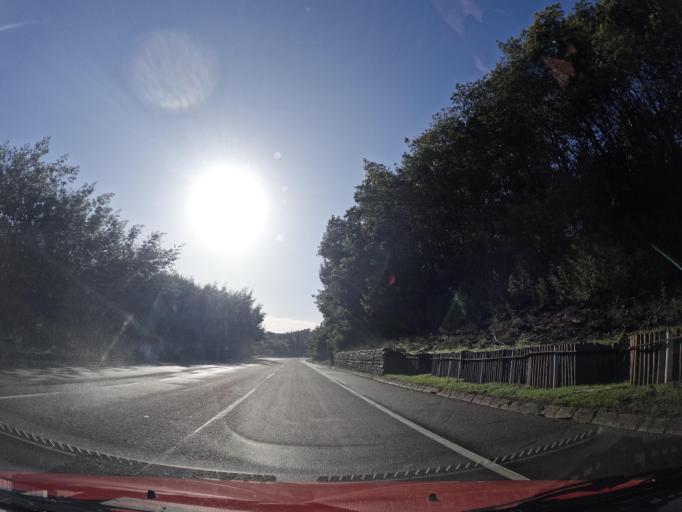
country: CL
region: Biobio
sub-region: Provincia de Concepcion
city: Penco
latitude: -36.7463
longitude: -72.9168
